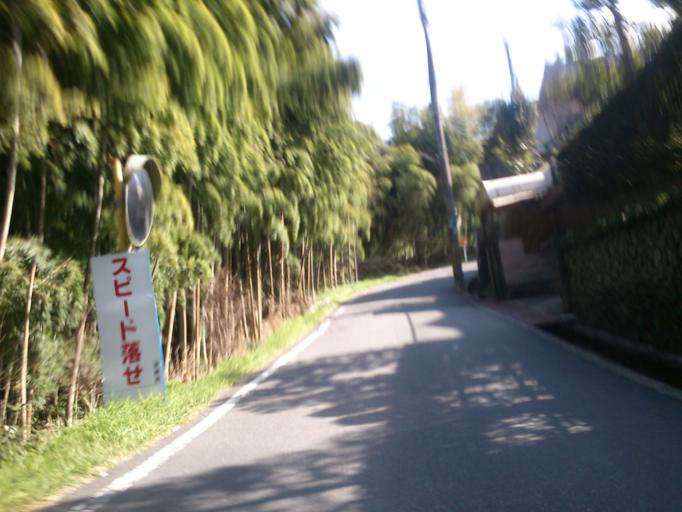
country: JP
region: Kyoto
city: Muko
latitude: 34.9208
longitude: 135.6695
